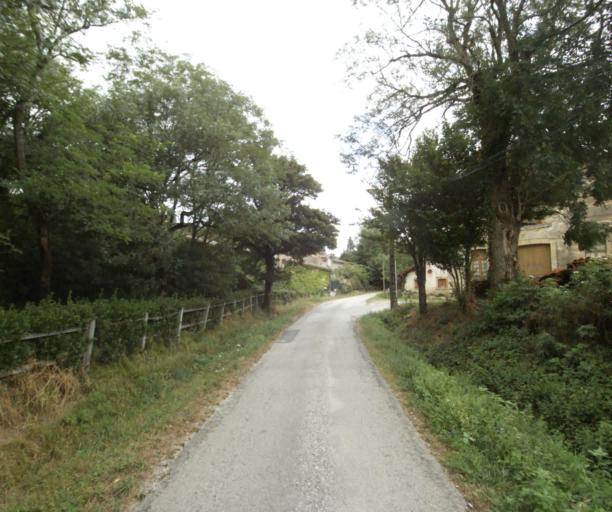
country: FR
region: Midi-Pyrenees
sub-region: Departement du Tarn
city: Soreze
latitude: 43.4574
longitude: 2.0824
